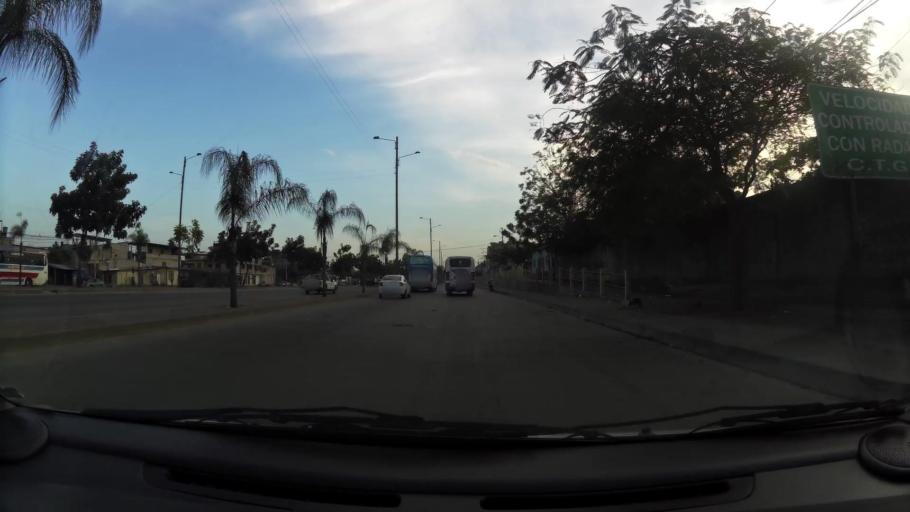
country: EC
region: Guayas
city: Eloy Alfaro
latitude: -2.1263
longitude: -79.8823
